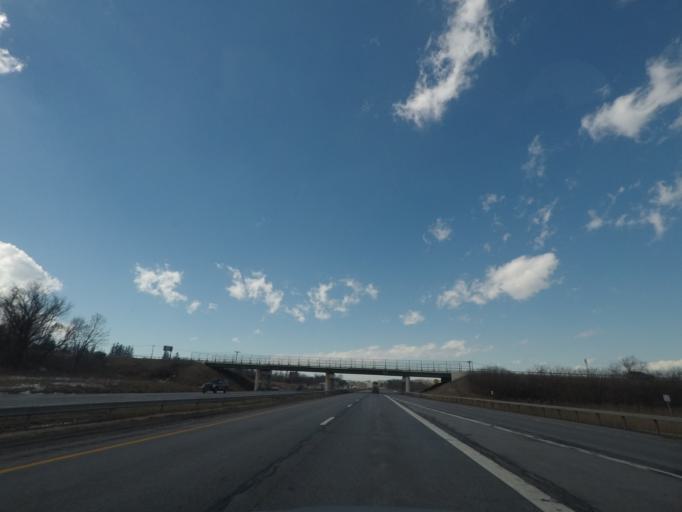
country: US
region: New York
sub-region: Montgomery County
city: Amsterdam
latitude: 42.9239
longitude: -74.2005
